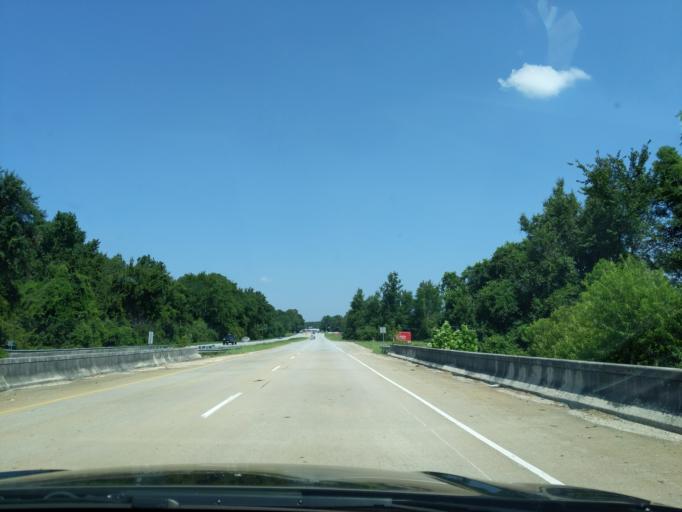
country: US
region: South Carolina
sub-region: Richland County
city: Forest Acres
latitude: 33.9552
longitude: -80.9807
